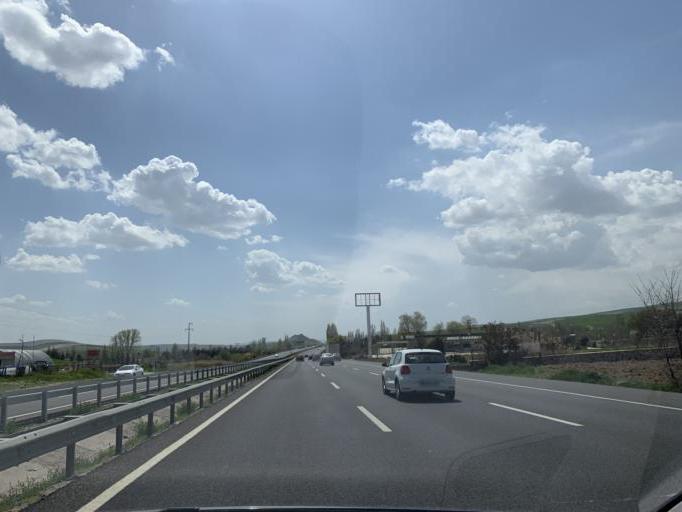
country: TR
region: Ankara
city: Temelli
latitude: 39.7933
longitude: 32.5293
